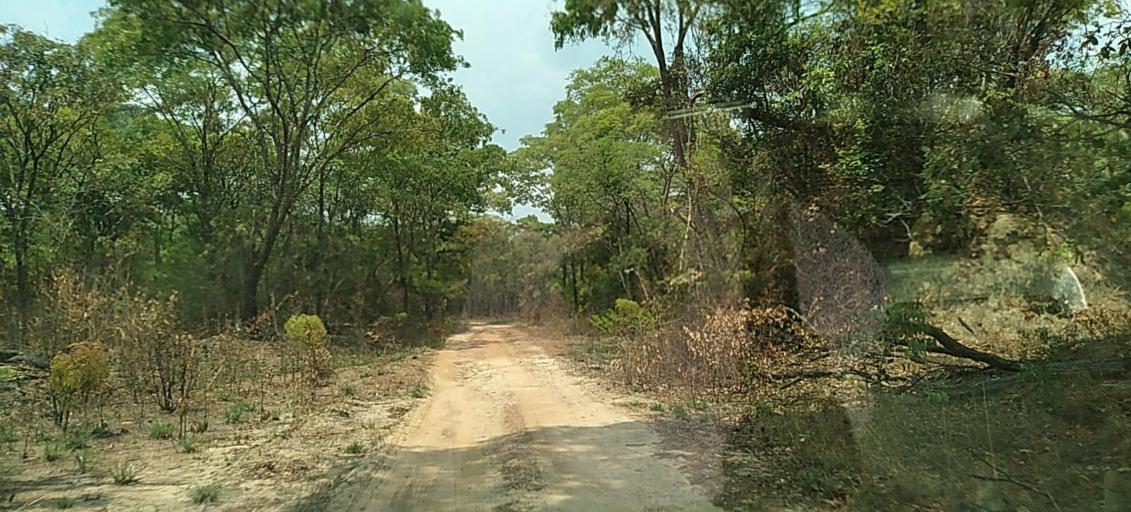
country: ZM
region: Copperbelt
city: Chingola
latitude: -12.7896
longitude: 27.6582
